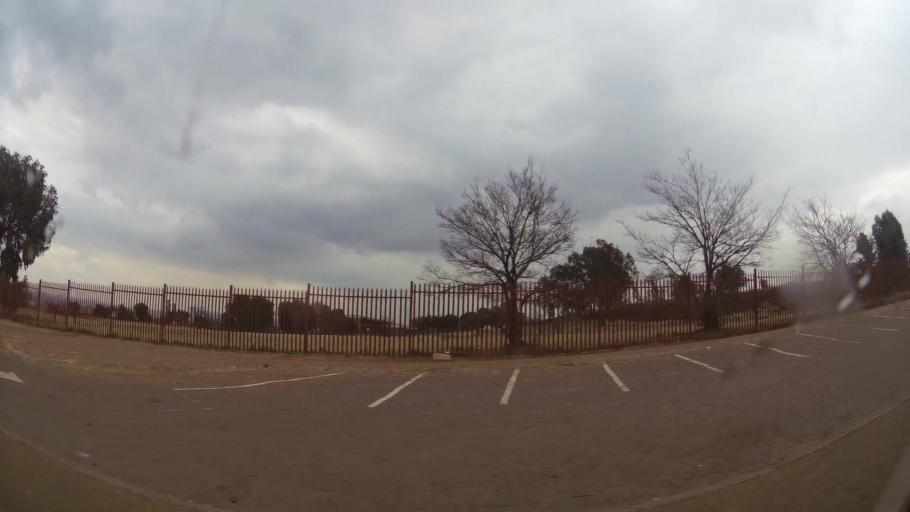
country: ZA
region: Gauteng
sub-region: Ekurhuleni Metropolitan Municipality
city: Germiston
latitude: -26.3798
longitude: 28.1270
